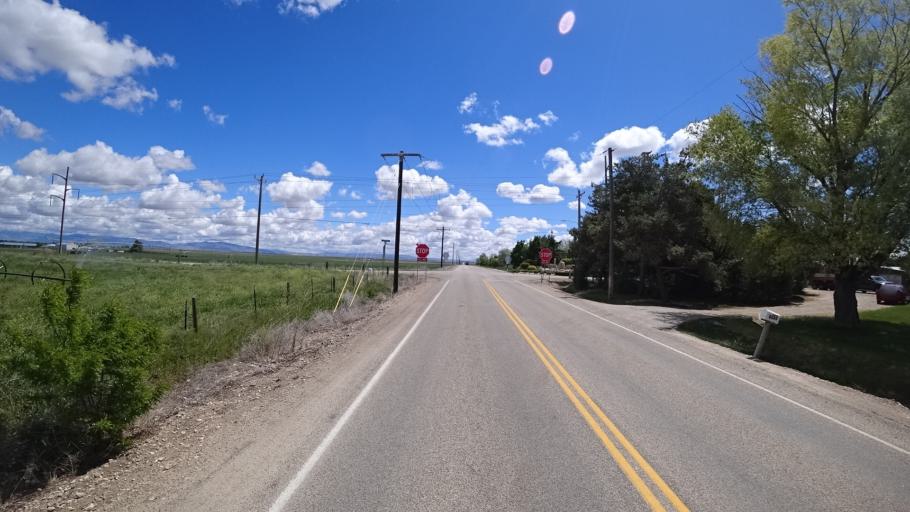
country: US
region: Idaho
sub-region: Ada County
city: Kuna
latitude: 43.4592
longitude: -116.3350
